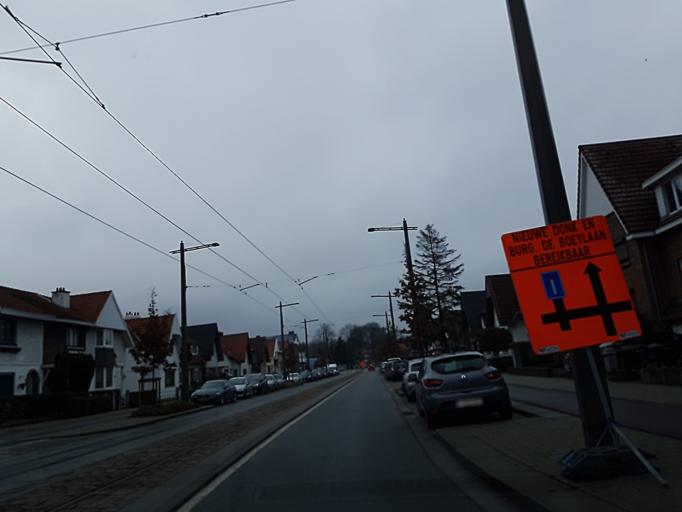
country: BE
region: Flanders
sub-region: Provincie Antwerpen
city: Borsbeek
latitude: 51.2076
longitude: 4.4721
